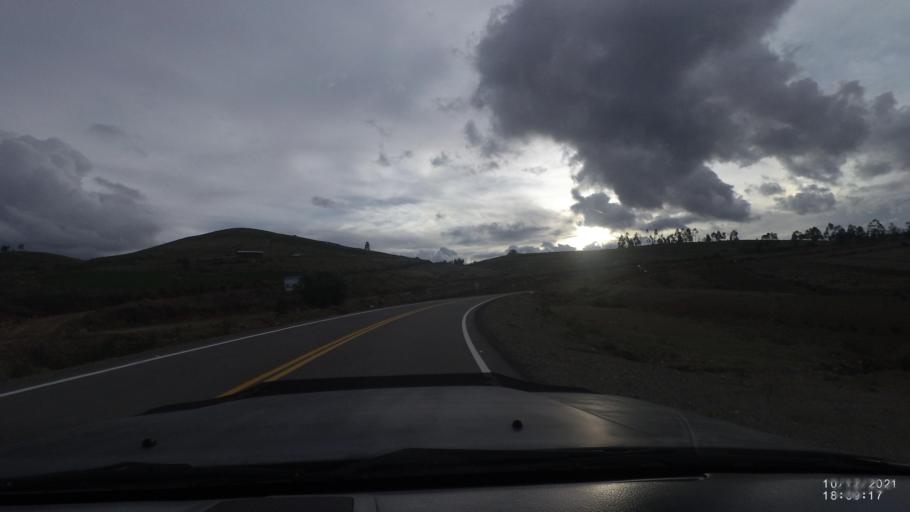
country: BO
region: Cochabamba
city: Tarata
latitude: -17.7934
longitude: -65.9495
